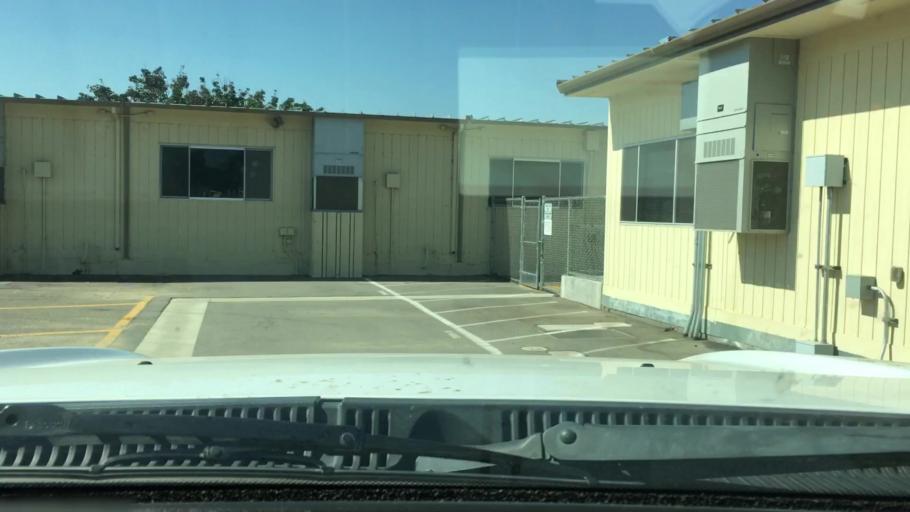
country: US
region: California
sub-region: San Luis Obispo County
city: San Luis Obispo
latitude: 35.2611
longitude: -120.6888
